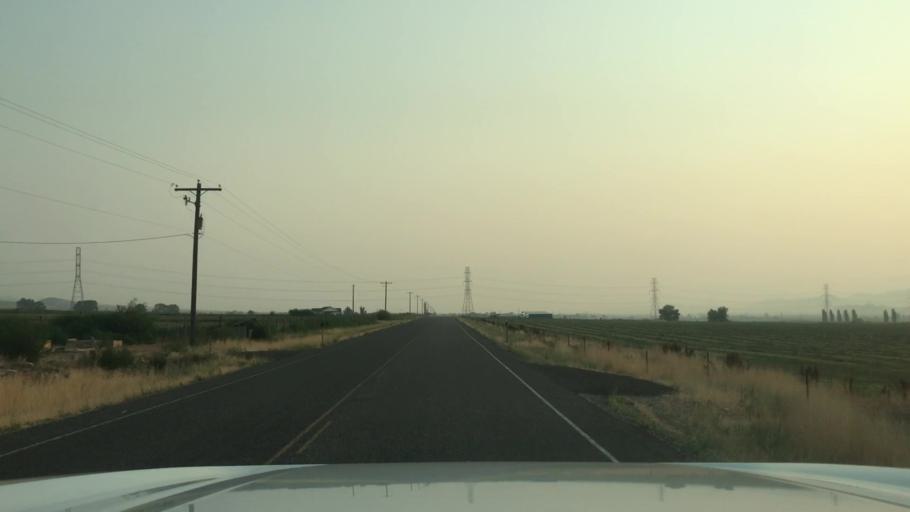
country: US
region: Utah
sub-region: Sevier County
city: Aurora
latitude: 38.8925
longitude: -111.9529
